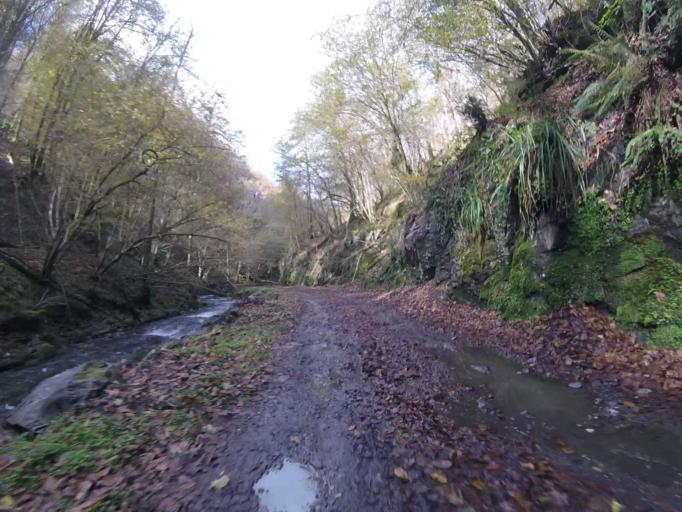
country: ES
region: Navarre
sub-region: Provincia de Navarra
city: Goizueta
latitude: 43.1889
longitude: -1.8011
